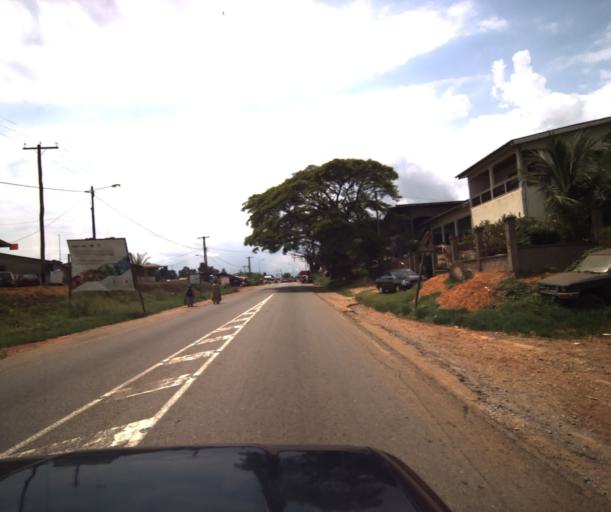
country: CM
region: Littoral
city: Edea
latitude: 3.7900
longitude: 10.1404
